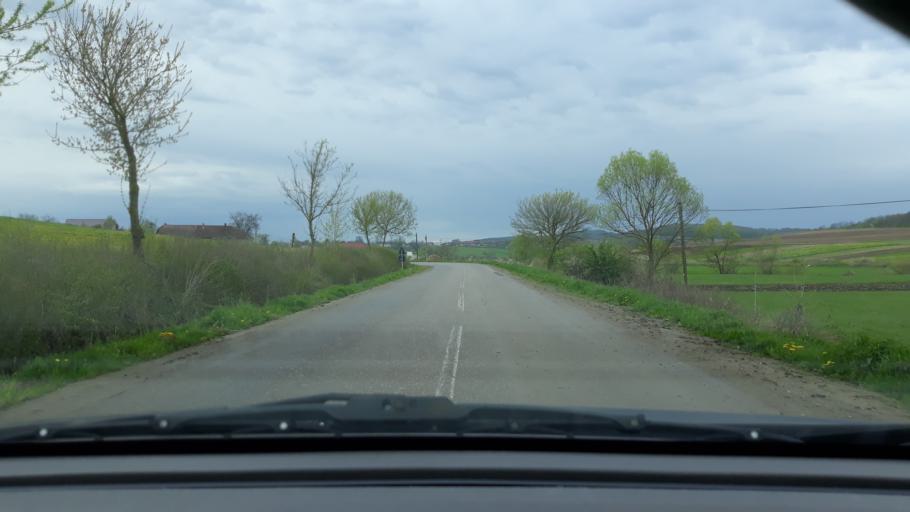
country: RO
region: Salaj
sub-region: Comuna Salatig
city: Salatig
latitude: 47.3772
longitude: 23.1433
